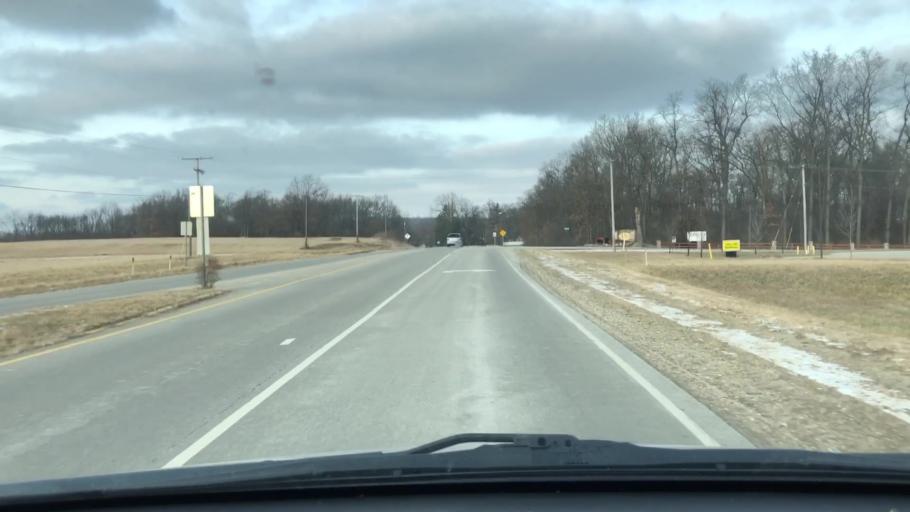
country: US
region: Indiana
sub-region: Steuben County
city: Angola
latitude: 41.6801
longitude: -85.0287
